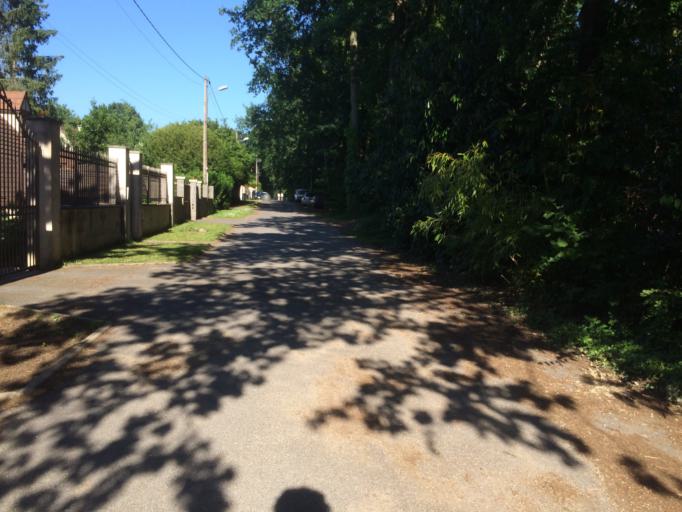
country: FR
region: Ile-de-France
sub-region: Departement du Val-de-Marne
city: Noiseau
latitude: 48.7536
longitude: 2.5532
